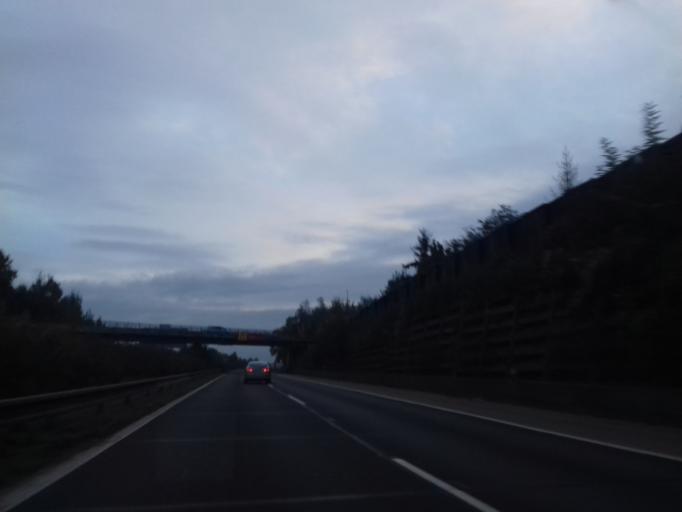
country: CZ
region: Praha
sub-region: Praha 20
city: Horni Pocernice
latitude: 50.1022
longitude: 14.6151
